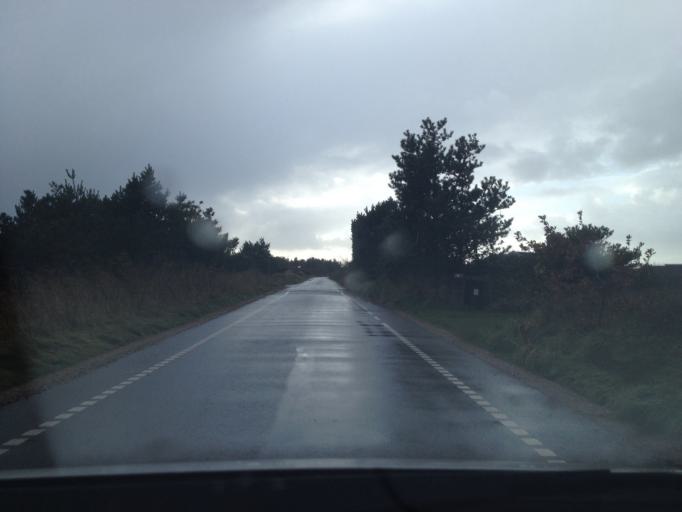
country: DE
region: Schleswig-Holstein
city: List
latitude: 55.1568
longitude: 8.5167
